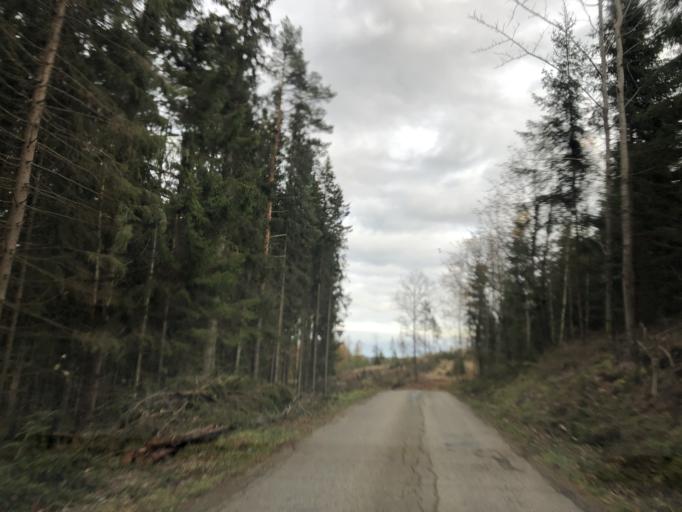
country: SE
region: Vaestra Goetaland
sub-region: Ulricehamns Kommun
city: Ulricehamn
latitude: 57.7259
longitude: 13.3608
